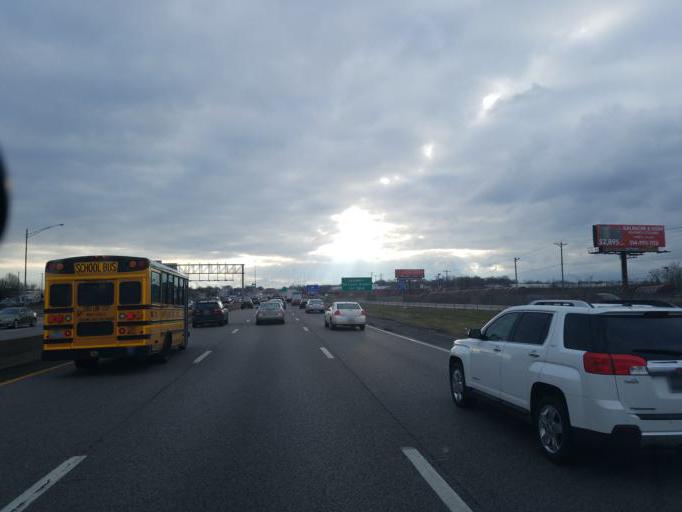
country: US
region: Missouri
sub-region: Saint Louis County
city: Hazelwood
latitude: 38.7770
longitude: -90.3535
